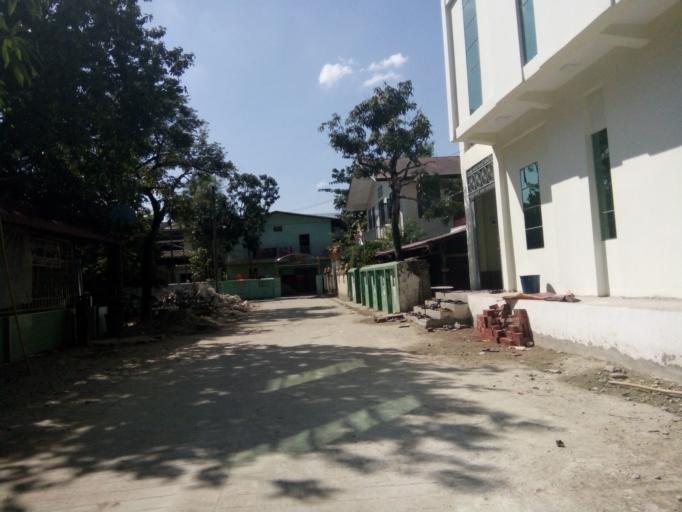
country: MM
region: Yangon
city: Yangon
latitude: 16.9198
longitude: 96.1590
